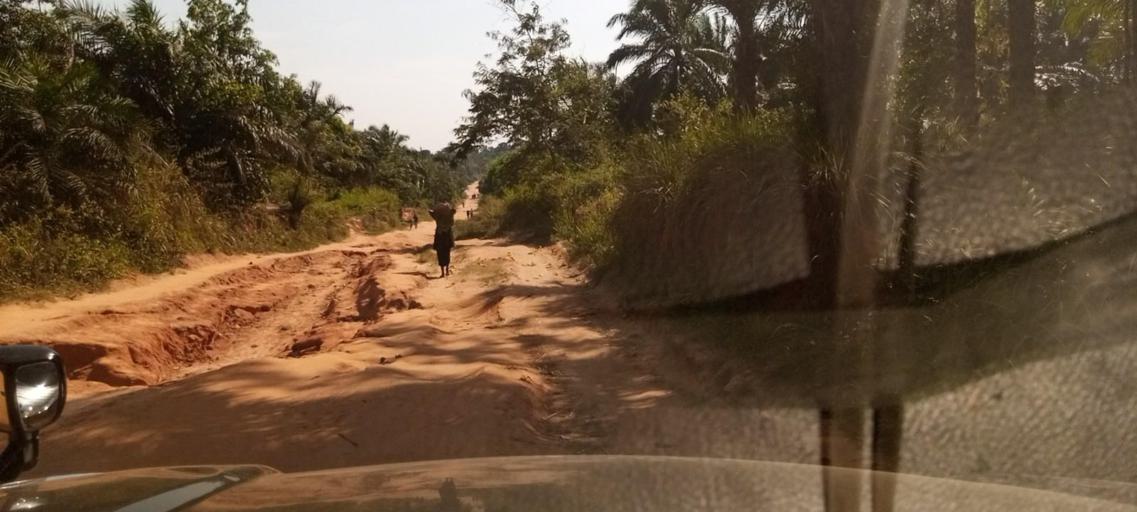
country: CD
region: Kasai-Oriental
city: Kabinda
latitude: -6.1189
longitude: 24.5276
